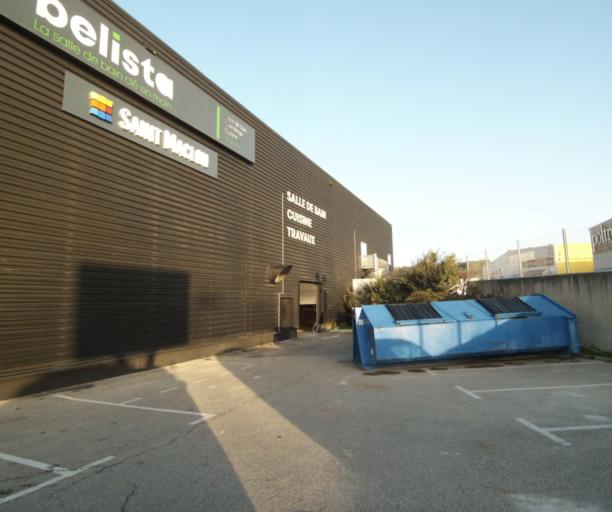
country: FR
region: Provence-Alpes-Cote d'Azur
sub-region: Departement des Bouches-du-Rhone
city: Septemes-les-Vallons
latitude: 43.4199
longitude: 5.3649
